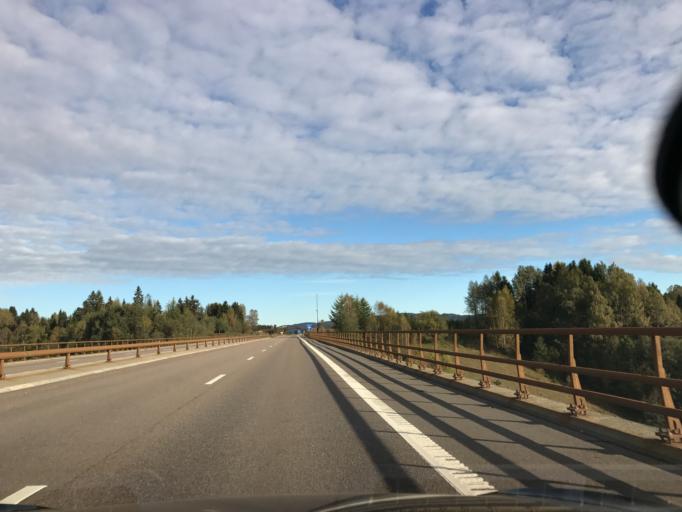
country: NO
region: Akershus
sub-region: Eidsvoll
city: Eidsvoll
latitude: 60.3756
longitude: 11.2077
